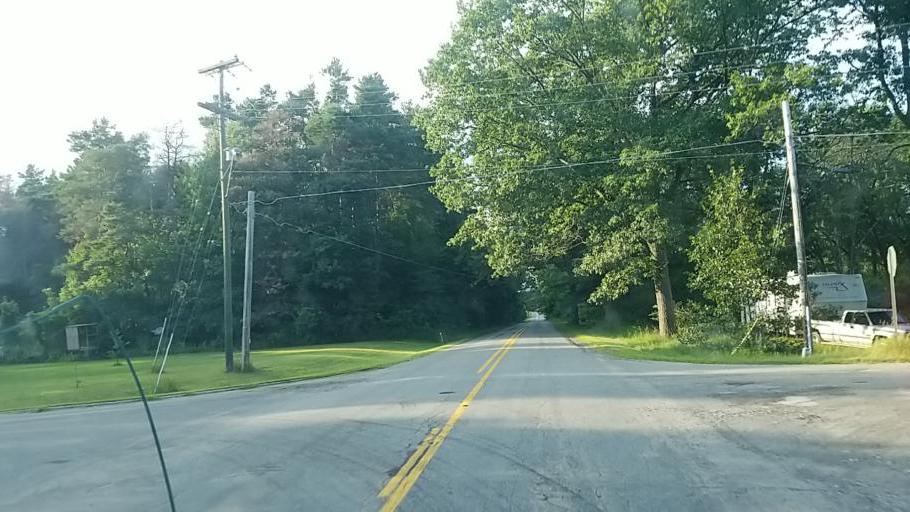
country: US
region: Michigan
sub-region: Montcalm County
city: Greenville
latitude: 43.2716
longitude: -85.3622
